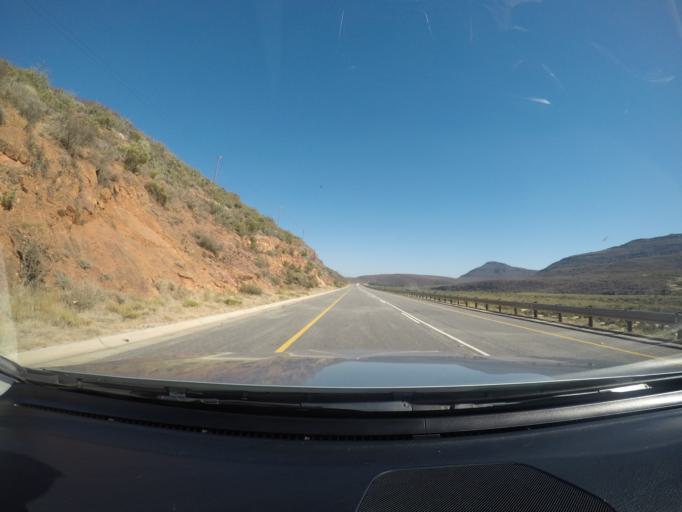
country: ZA
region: Western Cape
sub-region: West Coast District Municipality
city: Clanwilliam
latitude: -32.3918
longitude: 18.9494
